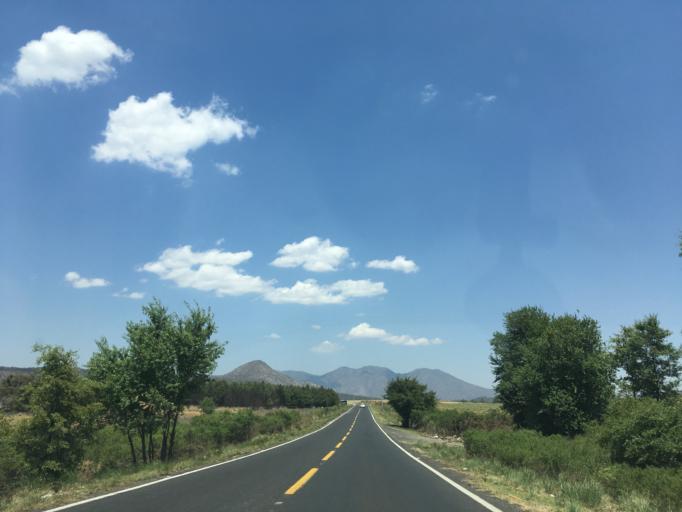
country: MX
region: Mexico
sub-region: Chalco
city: Zopoco
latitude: 19.7868
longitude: -102.0230
